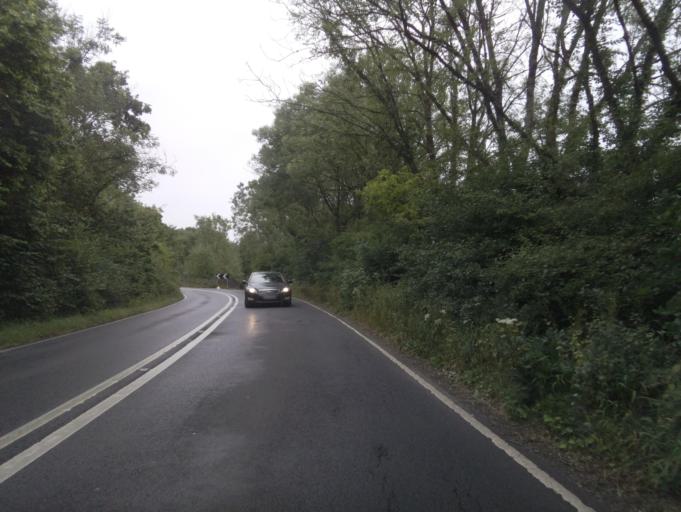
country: GB
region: England
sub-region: Devon
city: Axminster
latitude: 50.7982
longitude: -2.9817
